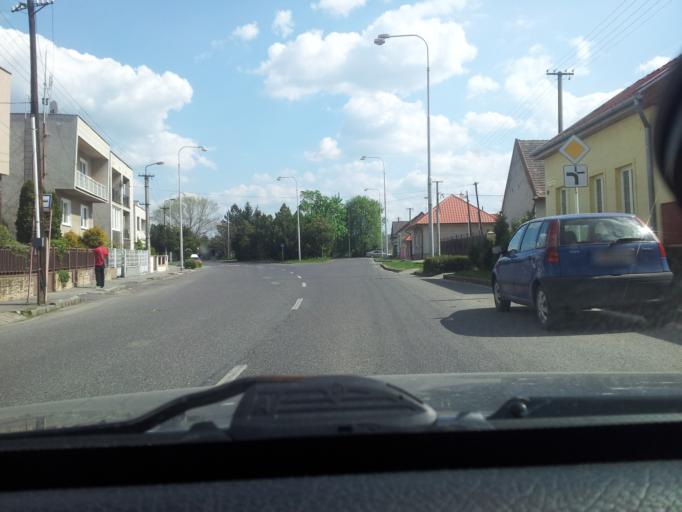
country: SK
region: Nitriansky
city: Levice
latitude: 48.2079
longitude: 18.6169
